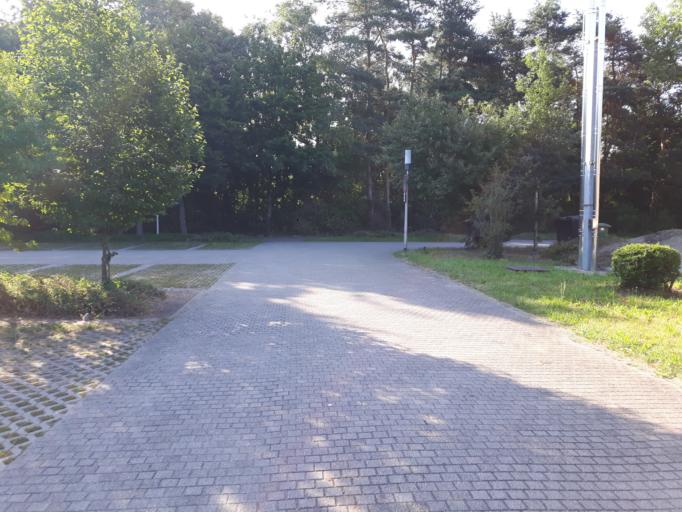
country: DE
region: Baden-Wuerttemberg
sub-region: Karlsruhe Region
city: Karlsdorf-Neuthard
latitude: 49.0966
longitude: 8.5318
